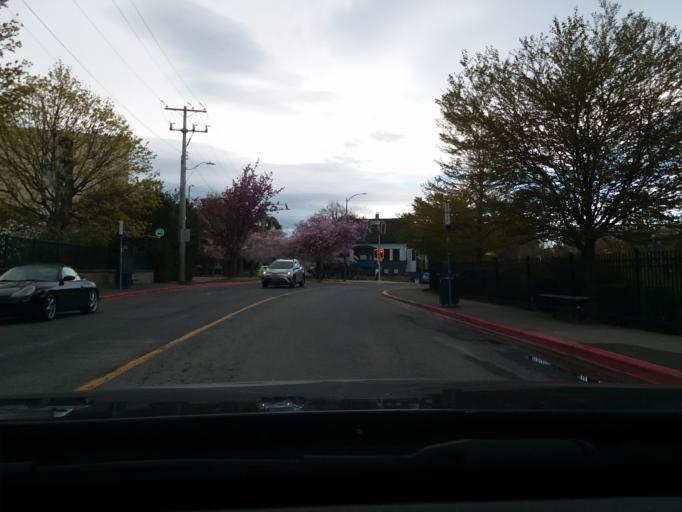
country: CA
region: British Columbia
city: Victoria
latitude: 48.4203
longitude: -123.3611
